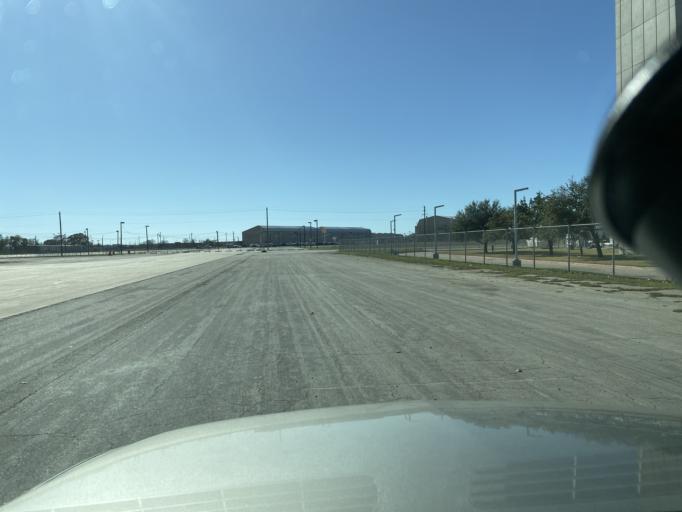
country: US
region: Texas
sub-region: Travis County
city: Hornsby Bend
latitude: 30.1961
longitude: -97.6650
